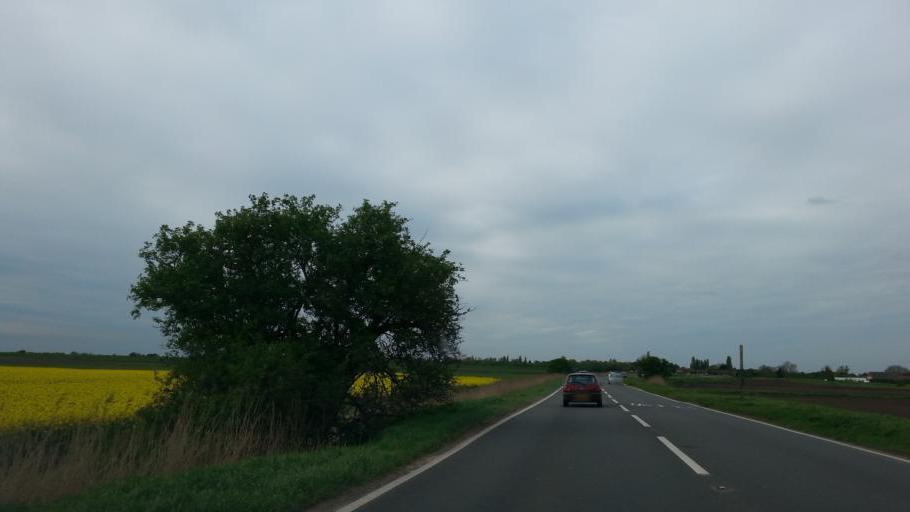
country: GB
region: England
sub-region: Cambridgeshire
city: March
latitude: 52.5949
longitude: 0.0602
